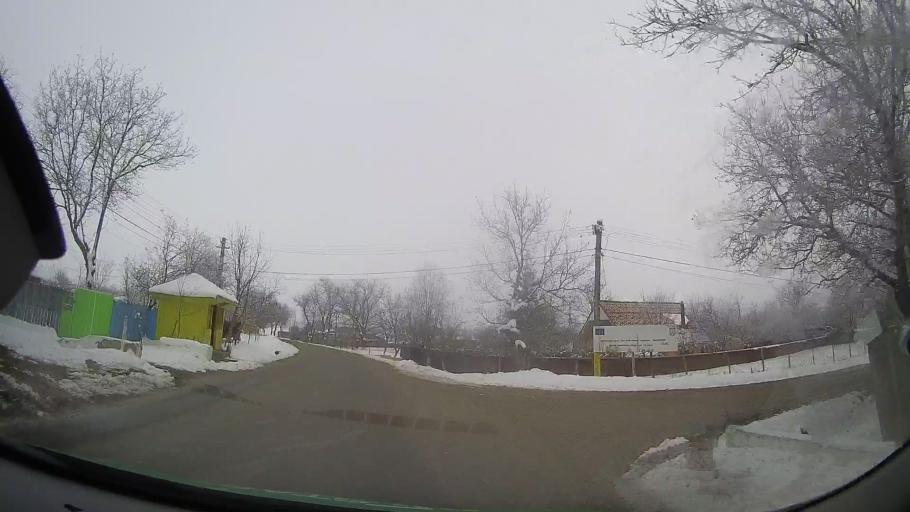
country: RO
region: Bacau
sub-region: Comuna Oncesti
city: Oncesti
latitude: 46.4517
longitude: 27.2620
